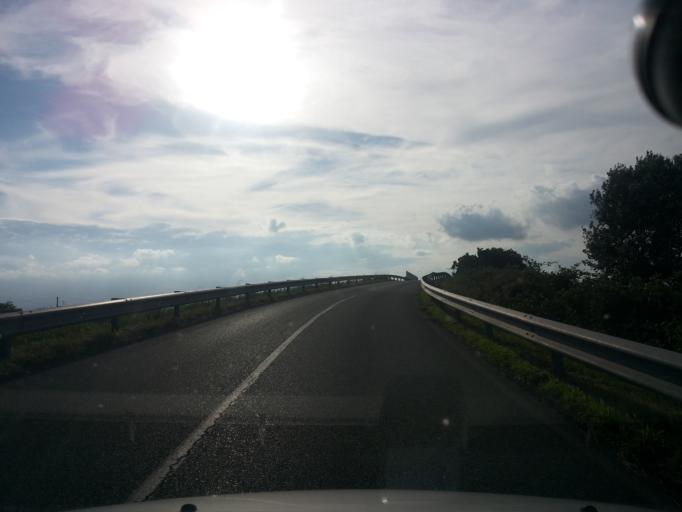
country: IT
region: Piedmont
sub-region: Provincia di Vercelli
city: Borgo Vercelli
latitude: 45.3623
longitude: 8.4658
